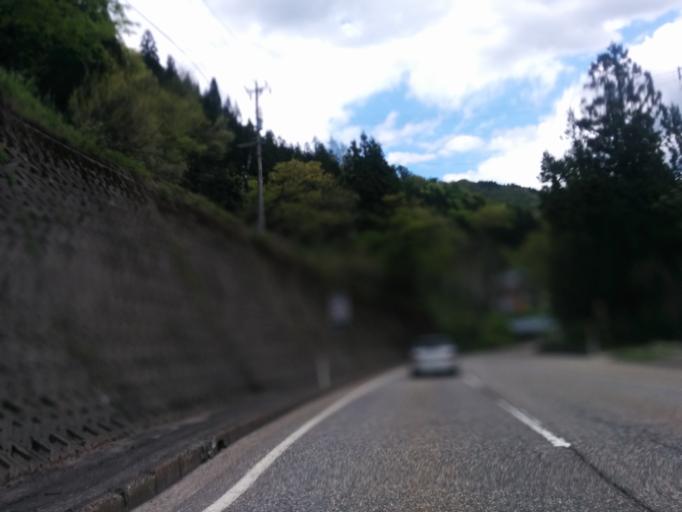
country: JP
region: Toyama
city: Nanto-shi
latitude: 36.4315
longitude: 136.9457
